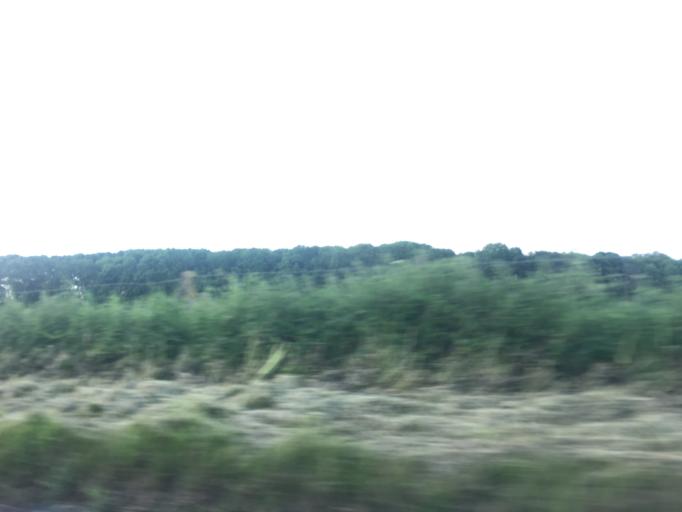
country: GB
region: England
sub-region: Leicestershire
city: Great Glen
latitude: 52.6122
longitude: -1.0374
